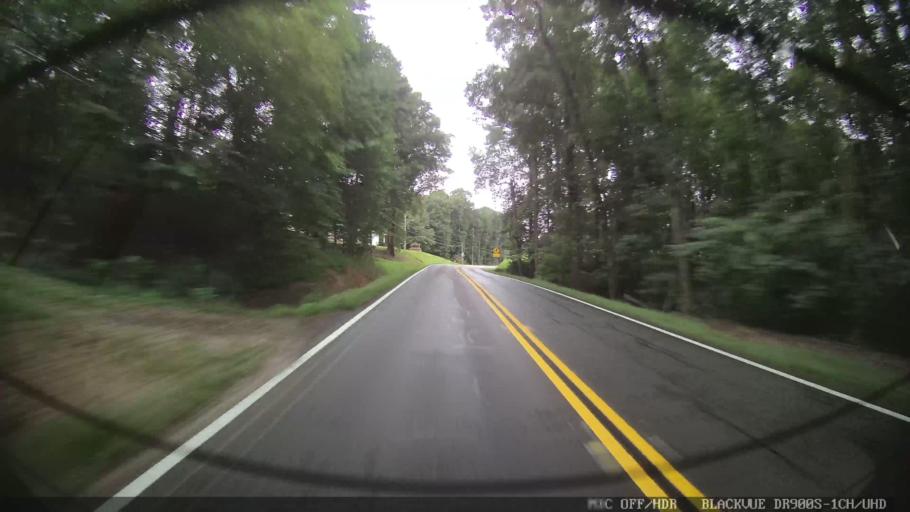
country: US
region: Georgia
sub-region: Gilmer County
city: Ellijay
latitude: 34.7338
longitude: -84.5130
